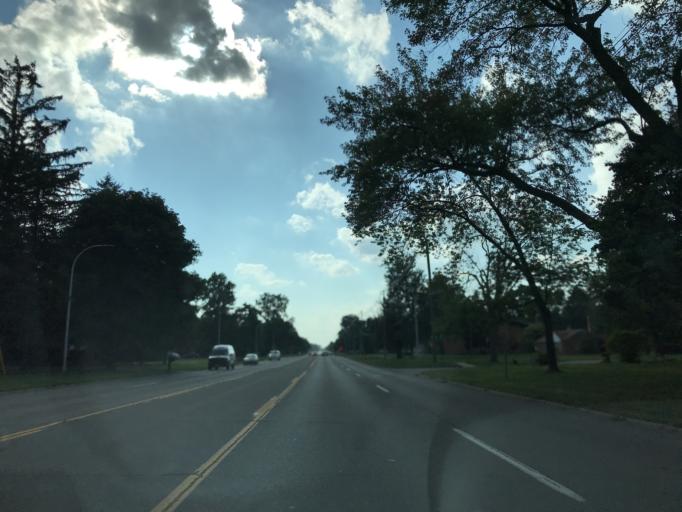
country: US
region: Michigan
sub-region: Wayne County
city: Livonia
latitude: 42.3981
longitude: -83.3372
